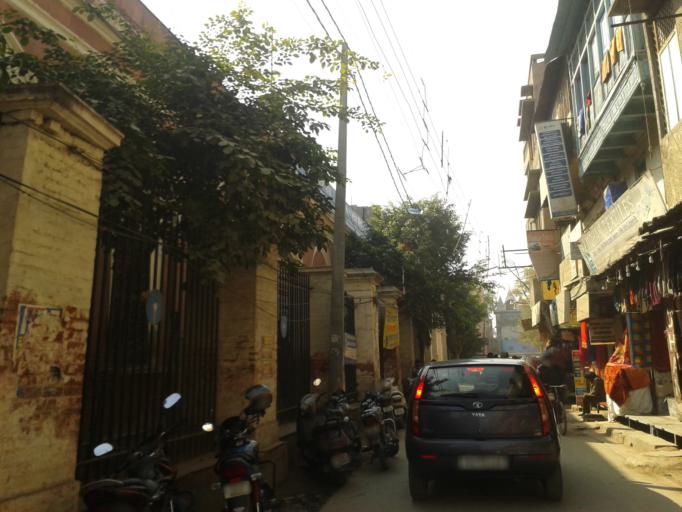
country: IN
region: Punjab
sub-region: Amritsar
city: Amritsar
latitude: 31.6257
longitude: 74.8801
